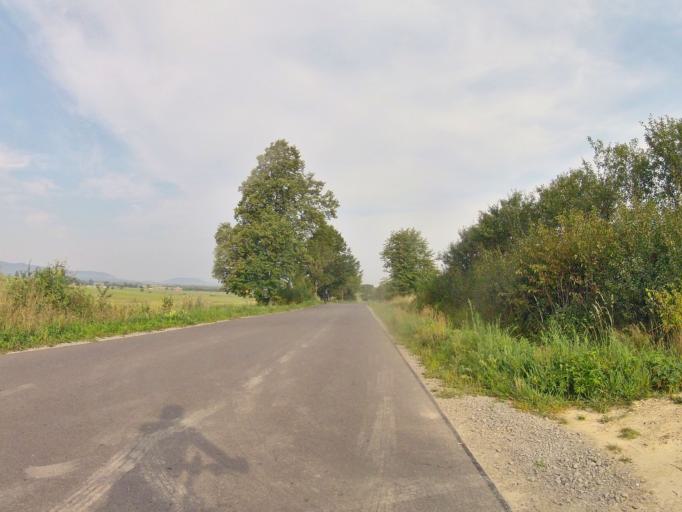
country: PL
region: Subcarpathian Voivodeship
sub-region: Powiat jasielski
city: Osiek Jasielski
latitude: 49.6263
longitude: 21.5054
